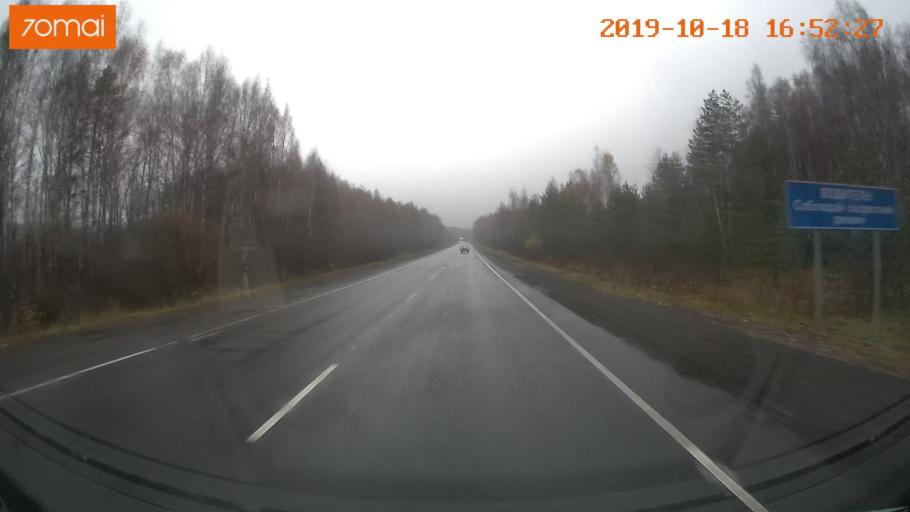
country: RU
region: Ivanovo
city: Nerl'
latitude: 56.6009
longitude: 40.5559
